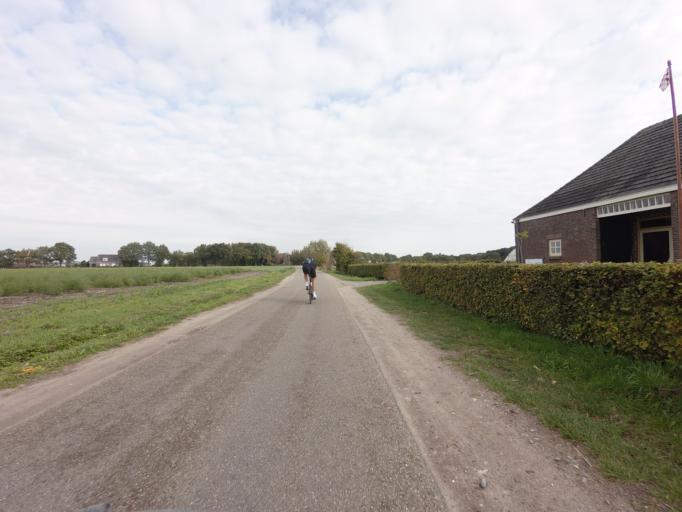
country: NL
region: North Brabant
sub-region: Gemeente Breda
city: Hoge Vucht
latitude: 51.6373
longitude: 4.7726
